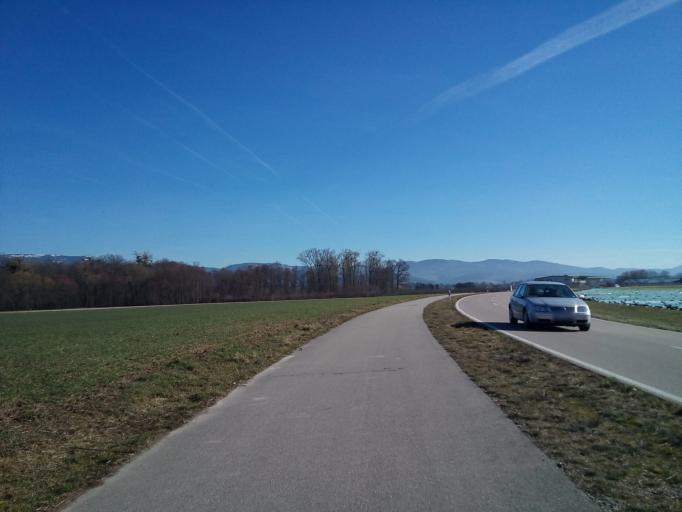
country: DE
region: Baden-Wuerttemberg
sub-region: Freiburg Region
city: Renchen
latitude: 48.6197
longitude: 8.0168
